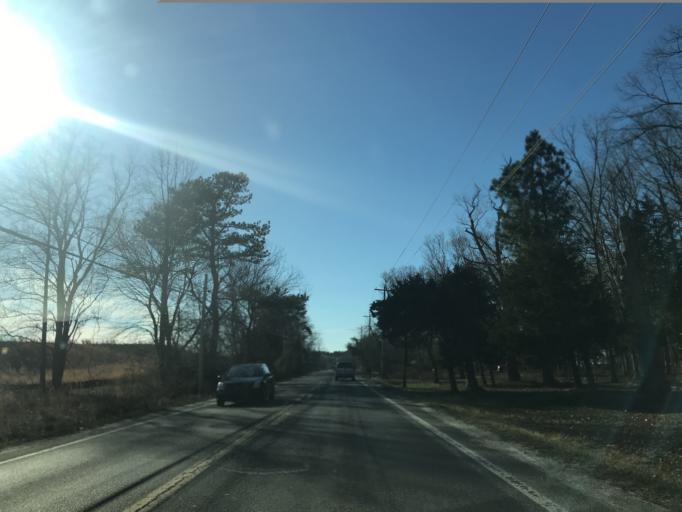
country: US
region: Maryland
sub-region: Prince George's County
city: Brandywine
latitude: 38.6900
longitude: -76.8964
